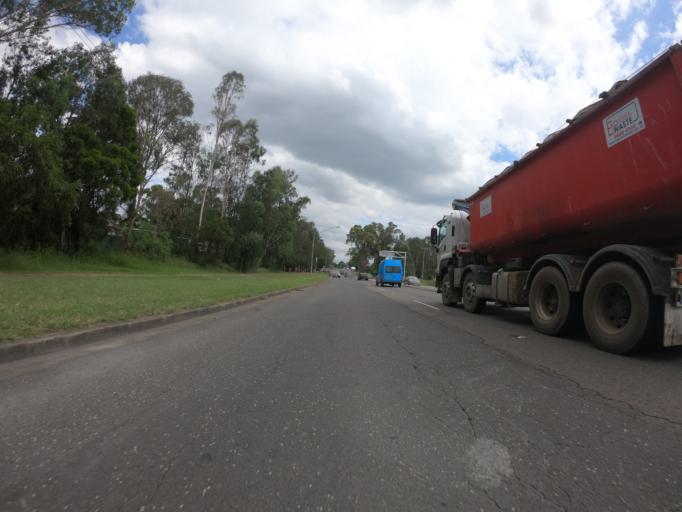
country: AU
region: New South Wales
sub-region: Blacktown
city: Mount Druitt
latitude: -33.7866
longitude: 150.7706
